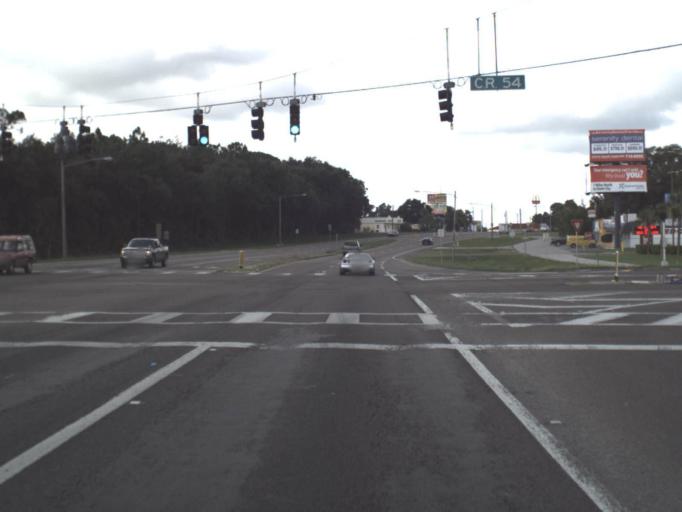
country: US
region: Florida
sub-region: Pasco County
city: Zephyrhills
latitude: 28.2521
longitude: -82.1883
